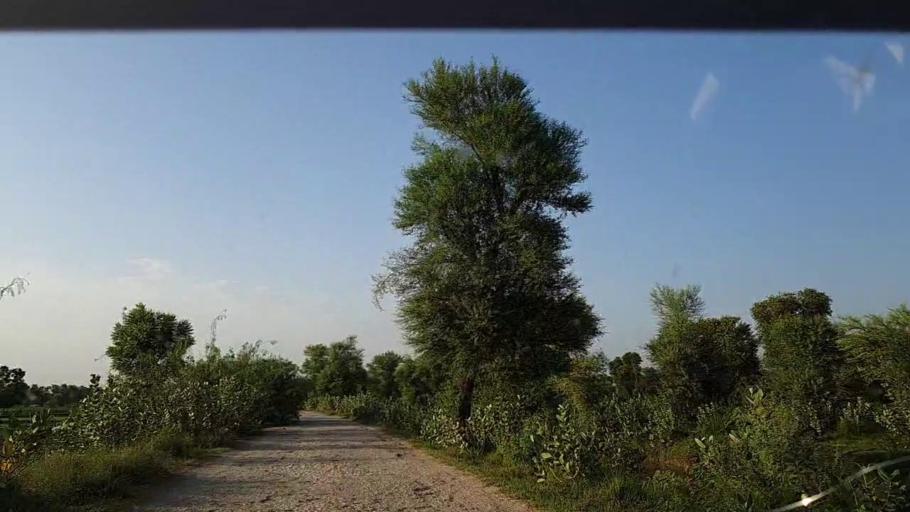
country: PK
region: Sindh
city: Pano Aqil
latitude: 27.9138
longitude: 69.2007
